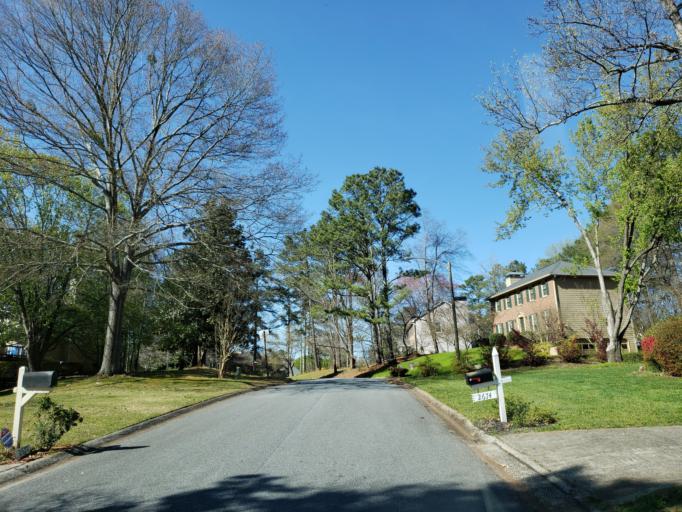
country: US
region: Georgia
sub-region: Cobb County
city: Marietta
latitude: 34.0129
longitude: -84.4851
